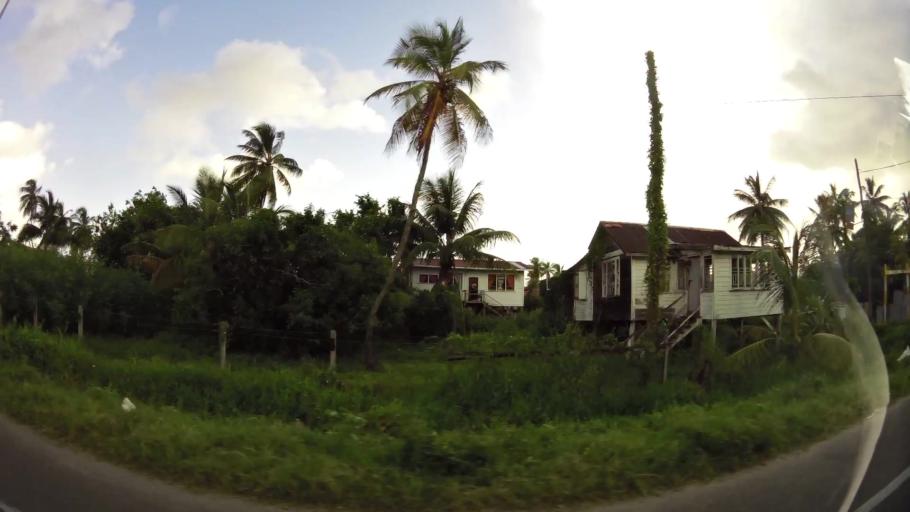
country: GY
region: Demerara-Mahaica
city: Georgetown
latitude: 6.7921
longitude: -58.0278
